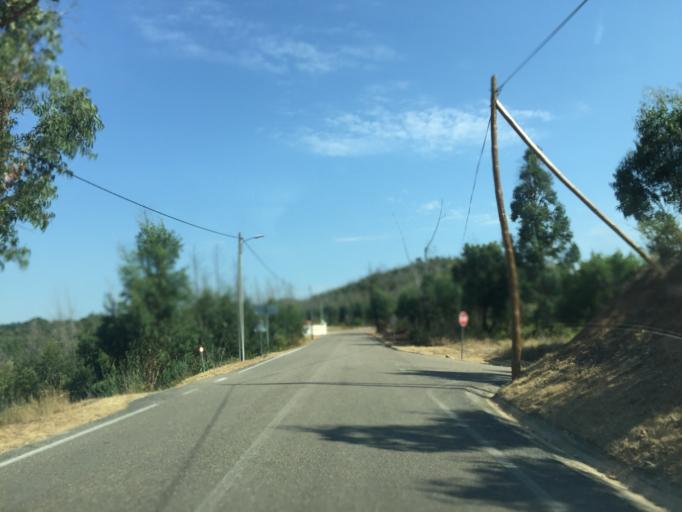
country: PT
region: Santarem
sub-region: Tomar
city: Tomar
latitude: 39.5784
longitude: -8.2973
